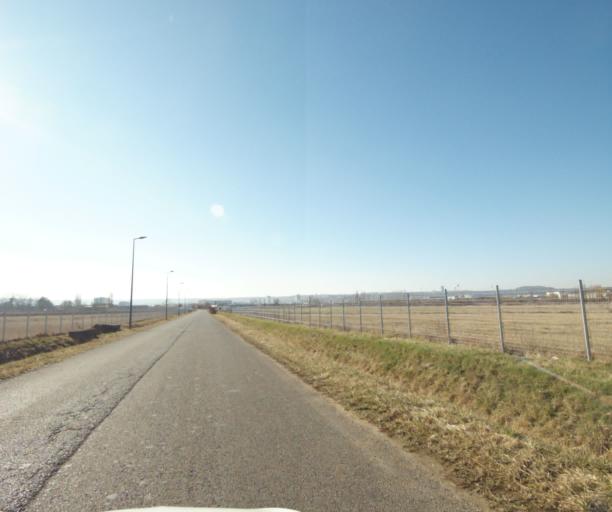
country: FR
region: Lorraine
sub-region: Departement de Meurthe-et-Moselle
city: Essey-les-Nancy
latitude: 48.6919
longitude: 6.2245
